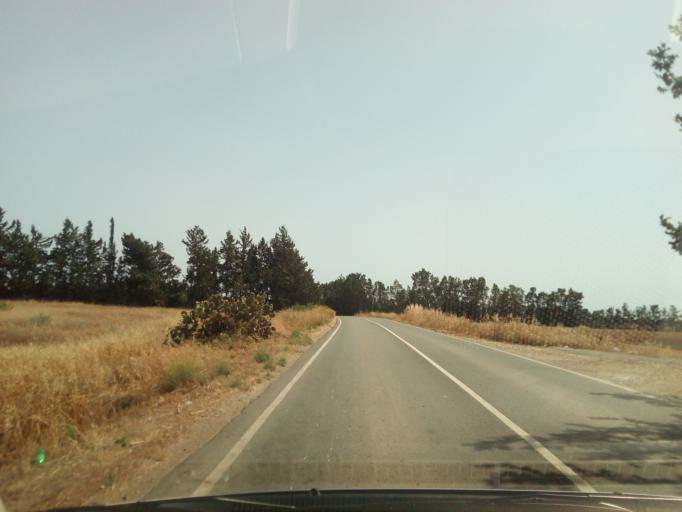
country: CY
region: Larnaka
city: Meneou
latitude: 34.8569
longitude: 33.5955
